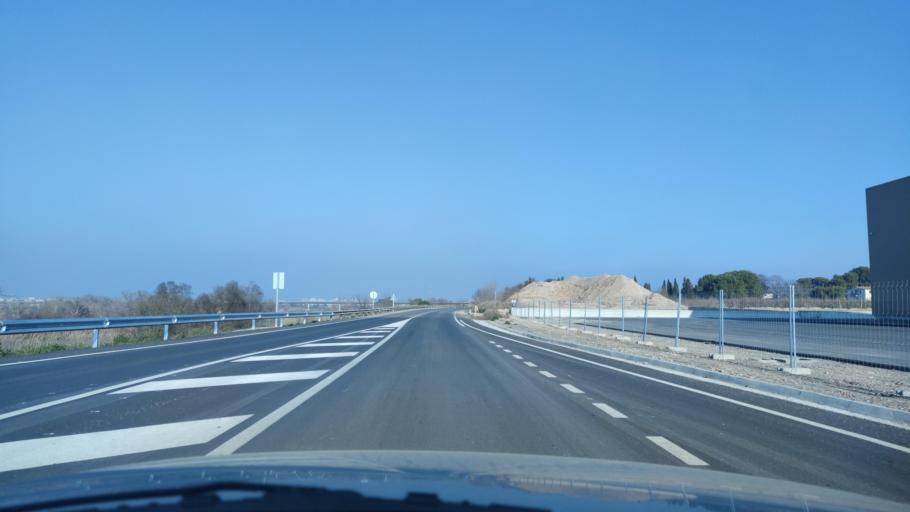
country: ES
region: Catalonia
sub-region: Provincia de Lleida
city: Lleida
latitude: 41.5798
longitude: 0.6160
